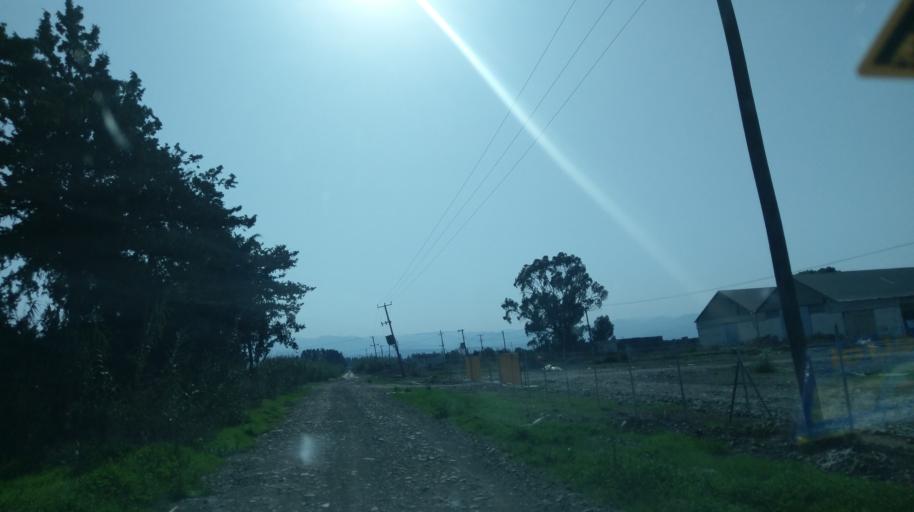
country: CY
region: Lefkosia
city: Morfou
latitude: 35.1977
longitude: 32.9346
